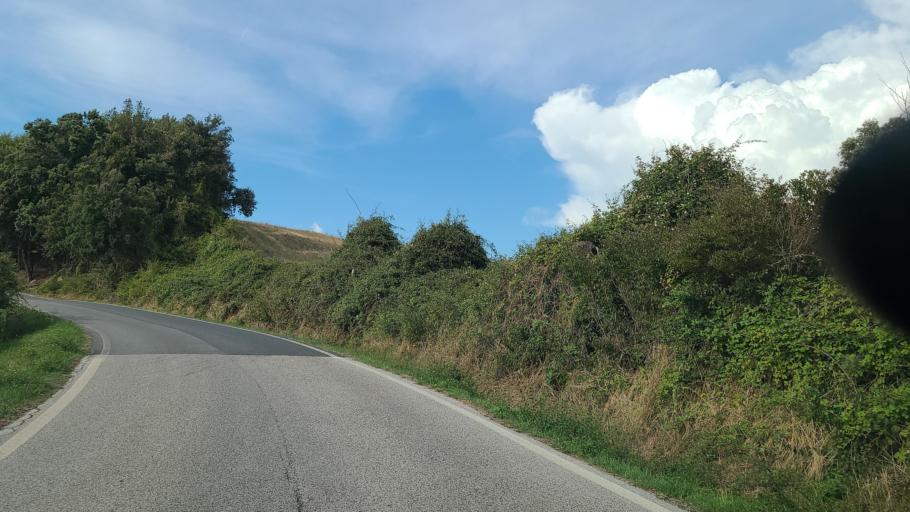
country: IT
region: Tuscany
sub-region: Provincia di Siena
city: San Gimignano
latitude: 43.4105
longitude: 10.9783
